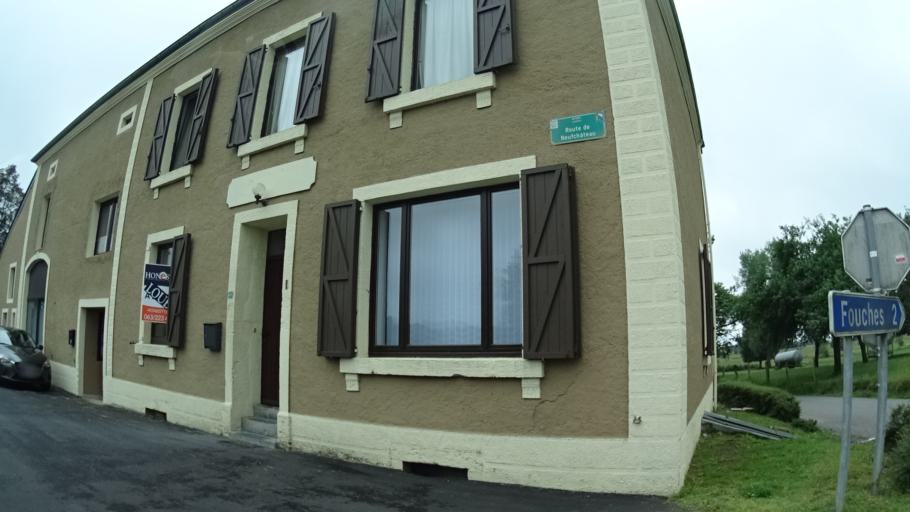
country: BE
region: Wallonia
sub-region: Province du Luxembourg
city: Attert
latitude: 49.7016
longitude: 5.7235
